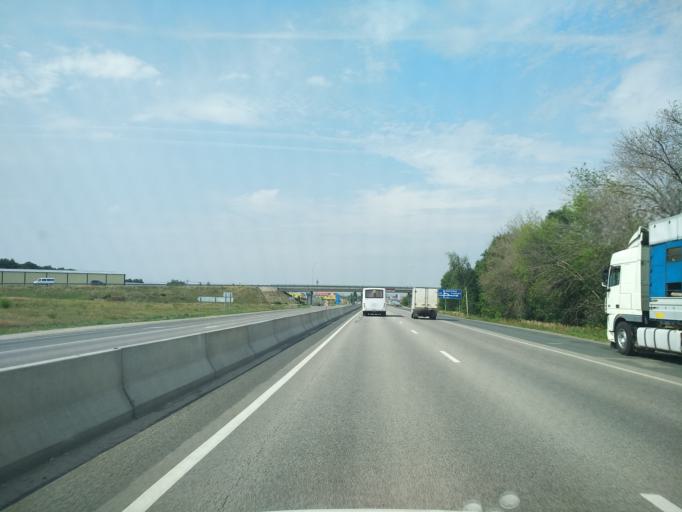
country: RU
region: Voronezj
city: Somovo
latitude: 51.6952
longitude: 39.3873
